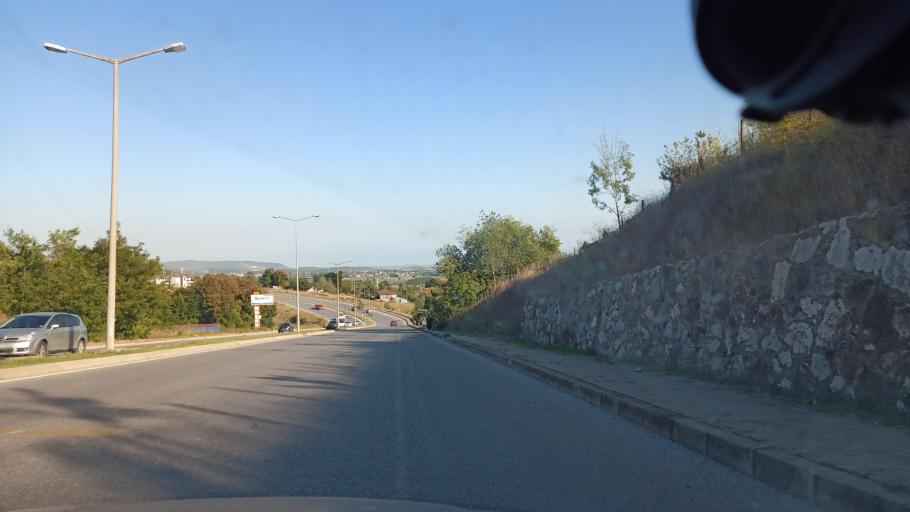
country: TR
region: Sakarya
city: Kazimpasa
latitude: 40.8540
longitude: 30.2987
